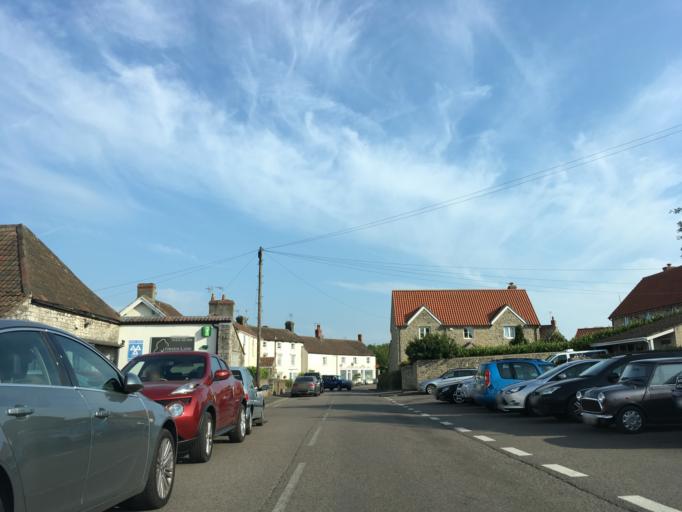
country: GB
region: England
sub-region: South Gloucestershire
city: Almondsbury
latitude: 51.5800
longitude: -2.5768
